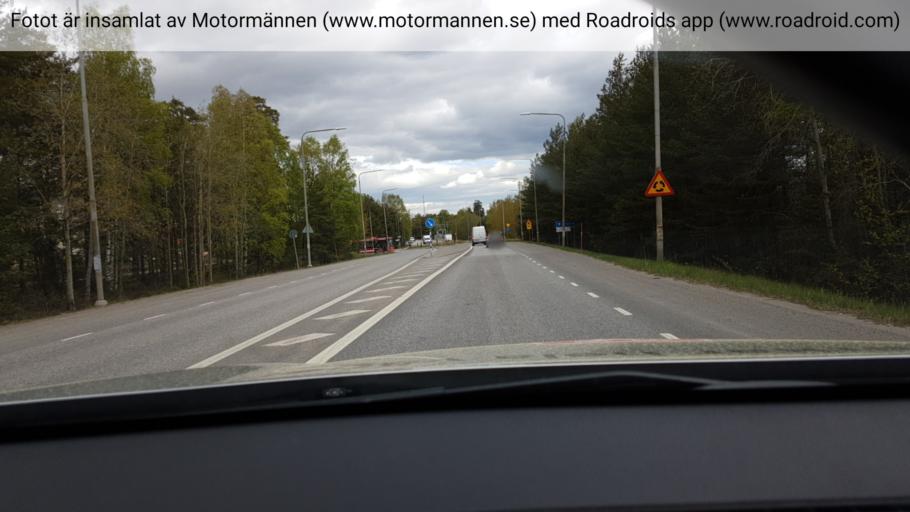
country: SE
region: Stockholm
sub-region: Haninge Kommun
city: Jordbro
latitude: 59.1372
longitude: 18.1228
